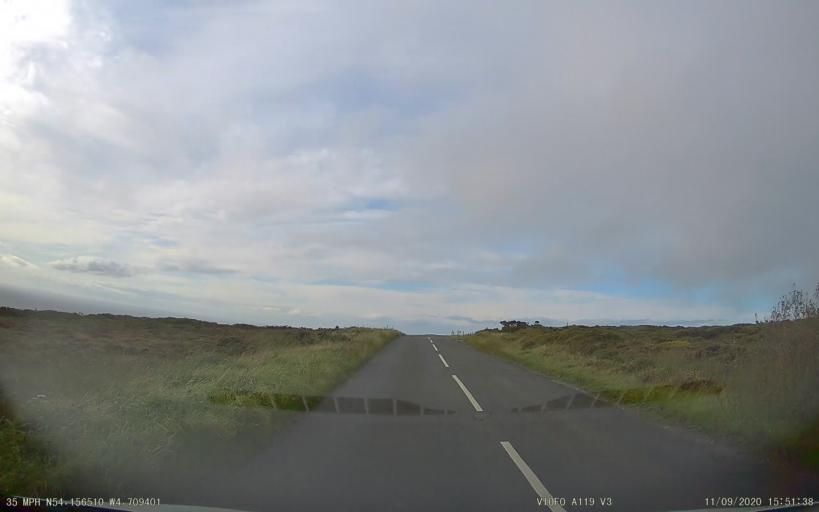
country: IM
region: Port Erin
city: Port Erin
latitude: 54.1565
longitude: -4.7094
